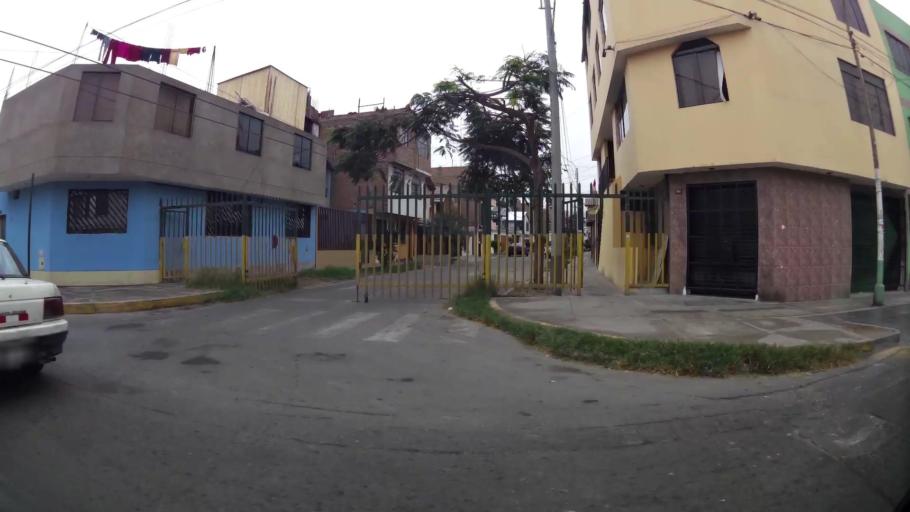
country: PE
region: Lima
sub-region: Lima
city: Independencia
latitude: -11.9664
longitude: -77.0709
